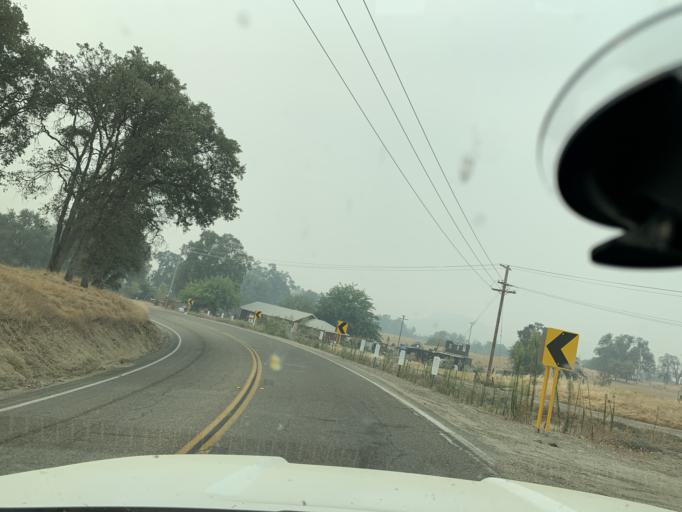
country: US
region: California
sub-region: Fresno County
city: Auberry
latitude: 37.0675
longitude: -119.4938
